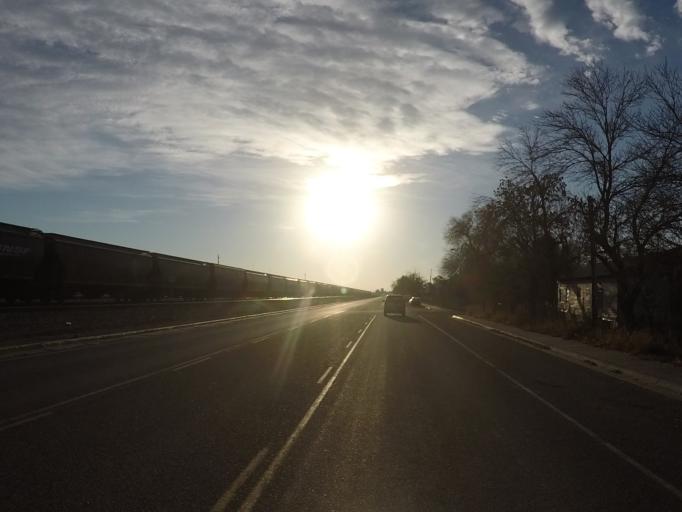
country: US
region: Montana
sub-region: Yellowstone County
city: Laurel
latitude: 45.6747
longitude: -108.7485
